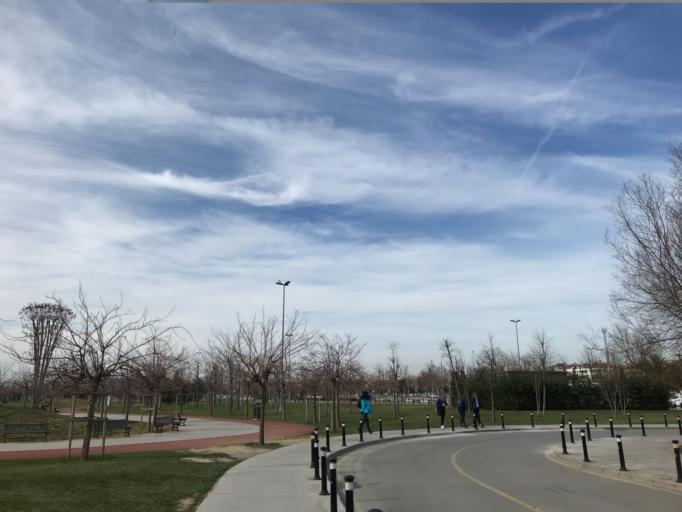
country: TR
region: Istanbul
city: Maltepe
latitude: 40.9336
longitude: 29.1152
